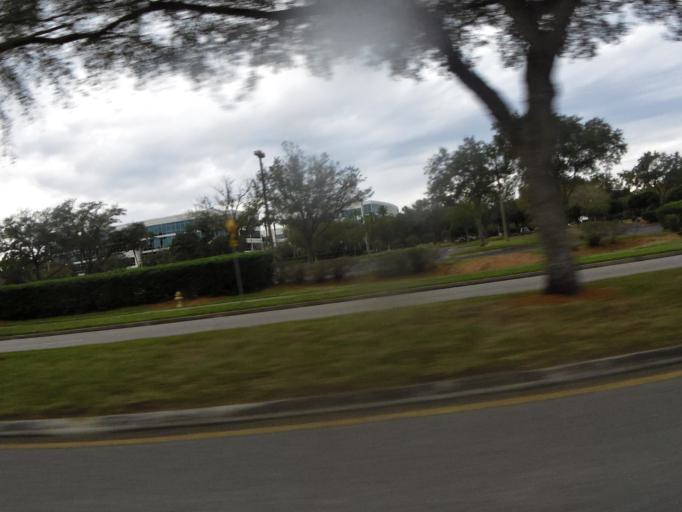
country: US
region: Florida
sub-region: Duval County
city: Jacksonville
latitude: 30.2423
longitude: -81.5840
